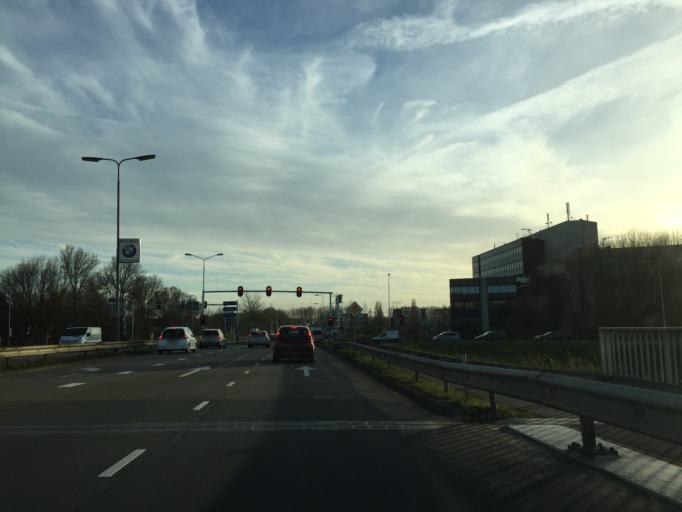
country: NL
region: North Brabant
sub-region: Gemeente 's-Hertogenbosch
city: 's-Hertogenbosch
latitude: 51.7177
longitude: 5.2960
